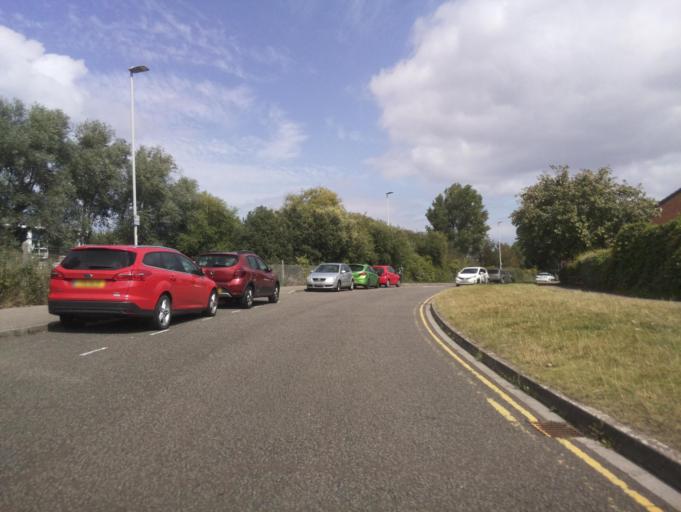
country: GB
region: England
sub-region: Poole
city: Poole
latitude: 50.7152
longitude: -1.9743
